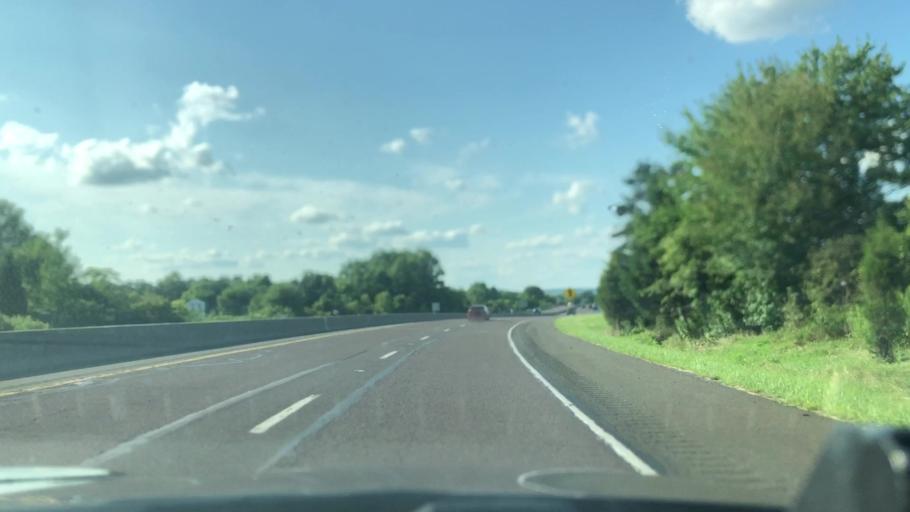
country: US
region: Pennsylvania
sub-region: Montgomery County
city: Souderton
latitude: 40.3181
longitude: -75.3088
